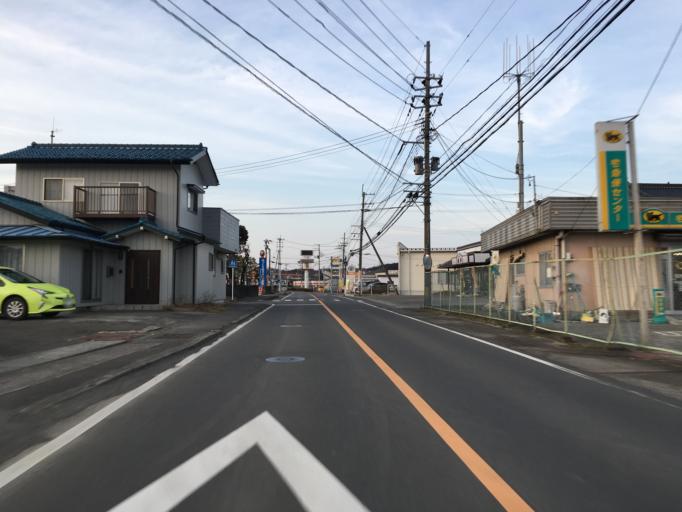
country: JP
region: Fukushima
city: Ishikawa
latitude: 37.0172
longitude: 140.3916
